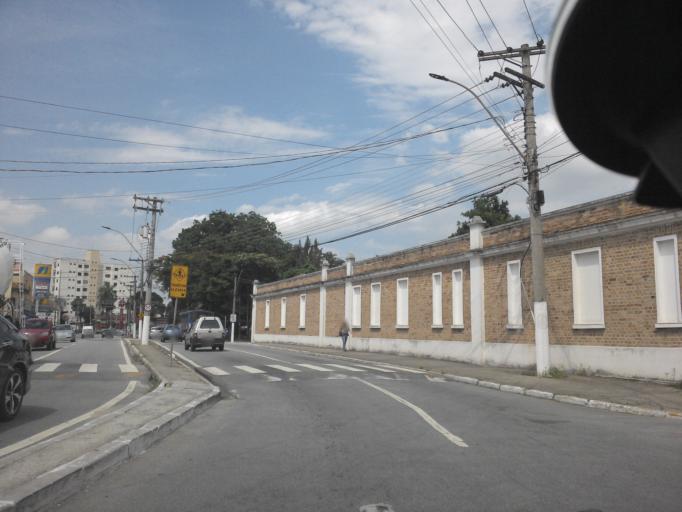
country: BR
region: Sao Paulo
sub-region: Taubate
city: Taubate
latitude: -23.0205
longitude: -45.5536
